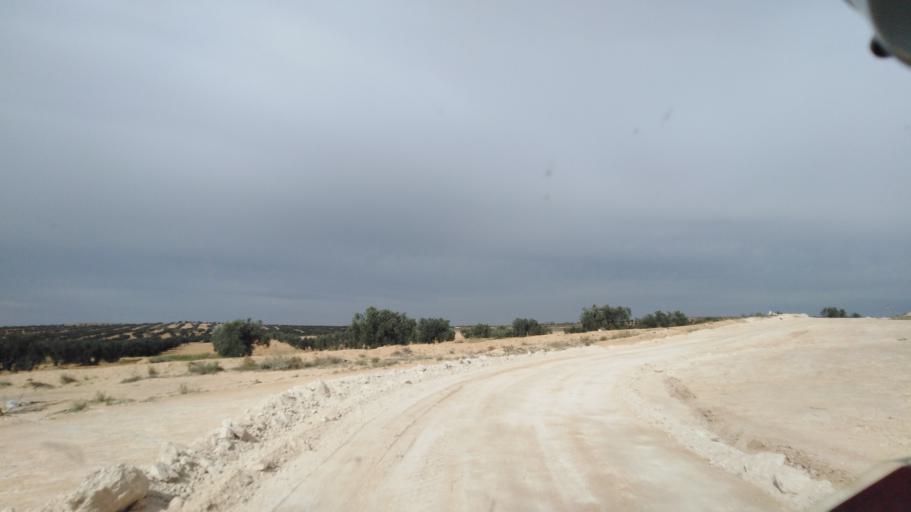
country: TN
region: Safaqis
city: Bi'r `Ali Bin Khalifah
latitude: 34.8153
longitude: 10.3072
